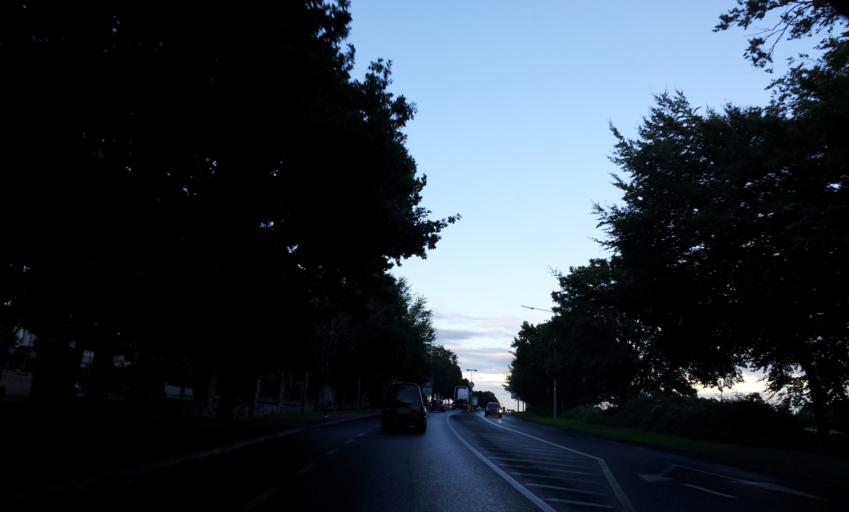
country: IE
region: Munster
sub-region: County Limerick
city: Newcastle West
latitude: 52.4510
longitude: -9.0468
